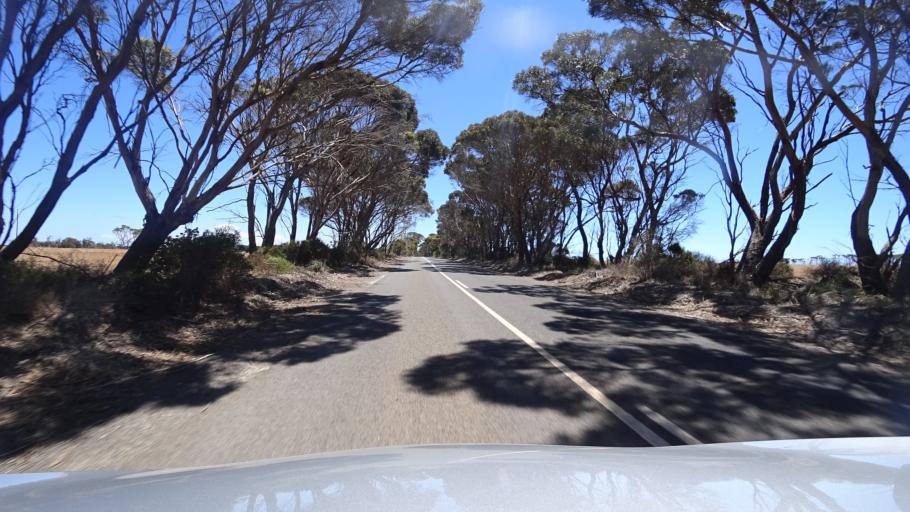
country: AU
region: South Australia
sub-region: Kangaroo Island
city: Kingscote
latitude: -35.7409
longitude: 137.9566
